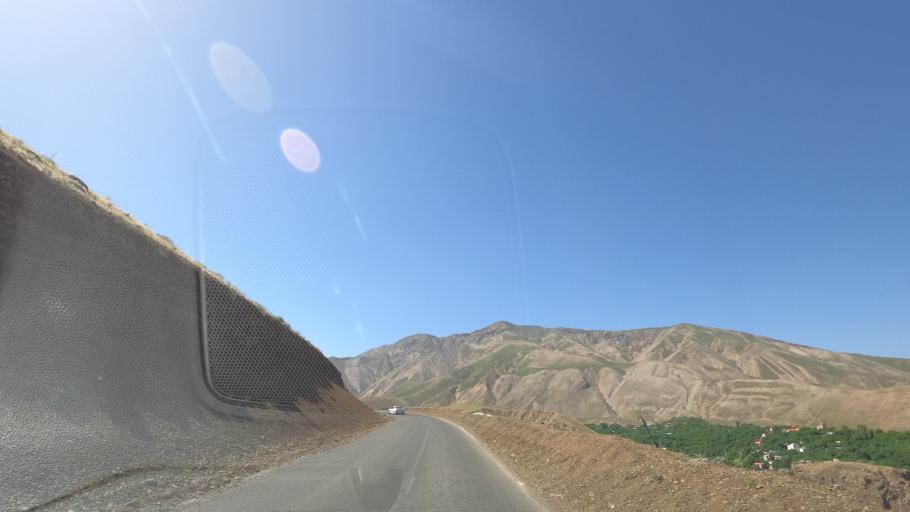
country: IR
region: Alborz
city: Karaj
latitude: 35.9338
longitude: 51.0823
